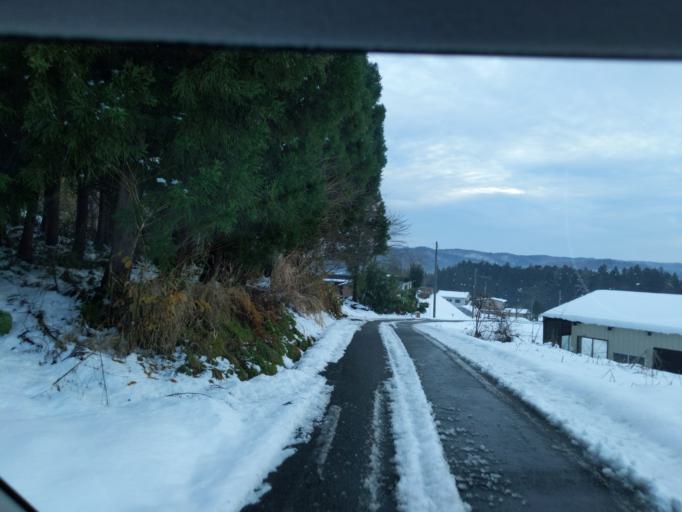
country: JP
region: Iwate
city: Mizusawa
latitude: 39.0500
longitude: 141.0577
